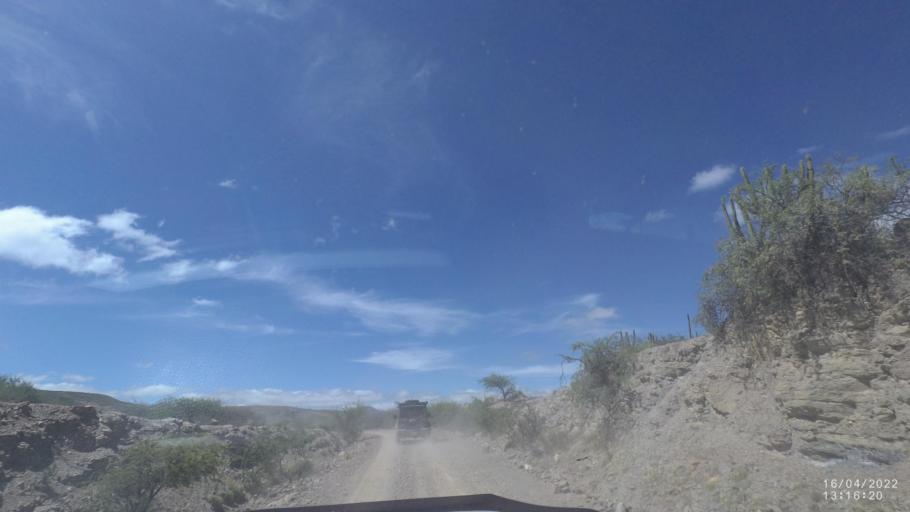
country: BO
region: Cochabamba
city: Mizque
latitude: -17.9889
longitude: -65.6248
